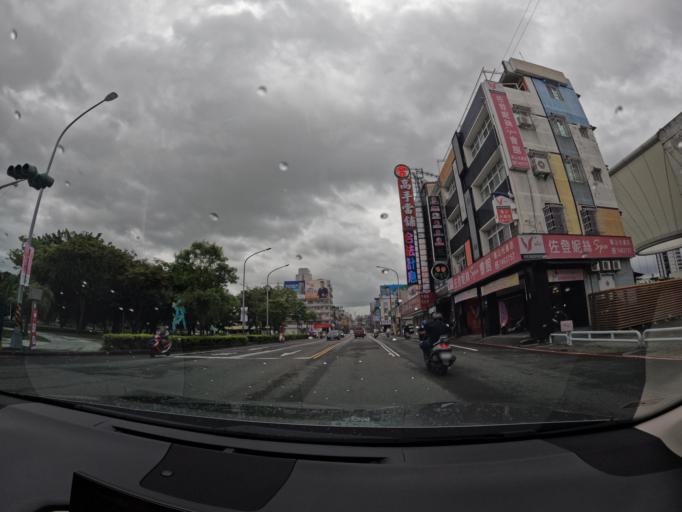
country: TW
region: Taiwan
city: Fengshan
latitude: 22.6250
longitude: 120.3642
